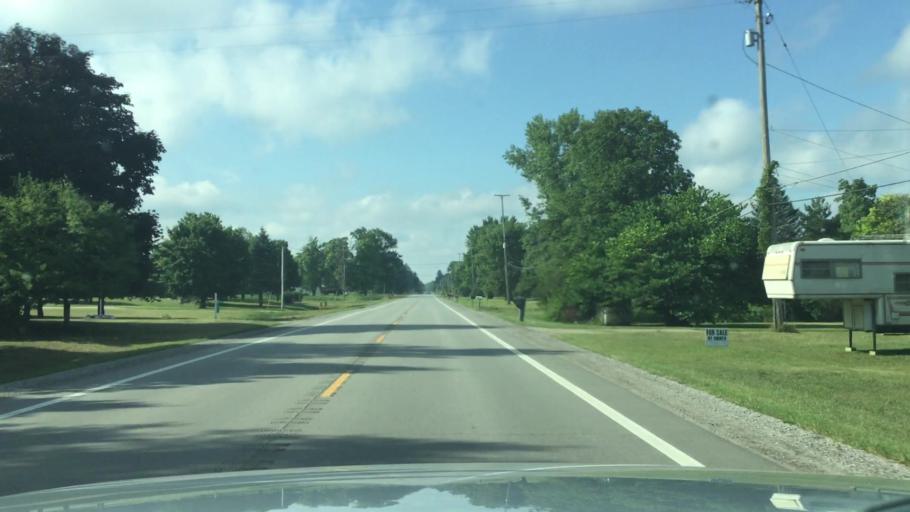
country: US
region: Michigan
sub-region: Saginaw County
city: Birch Run
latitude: 43.2431
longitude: -83.7354
